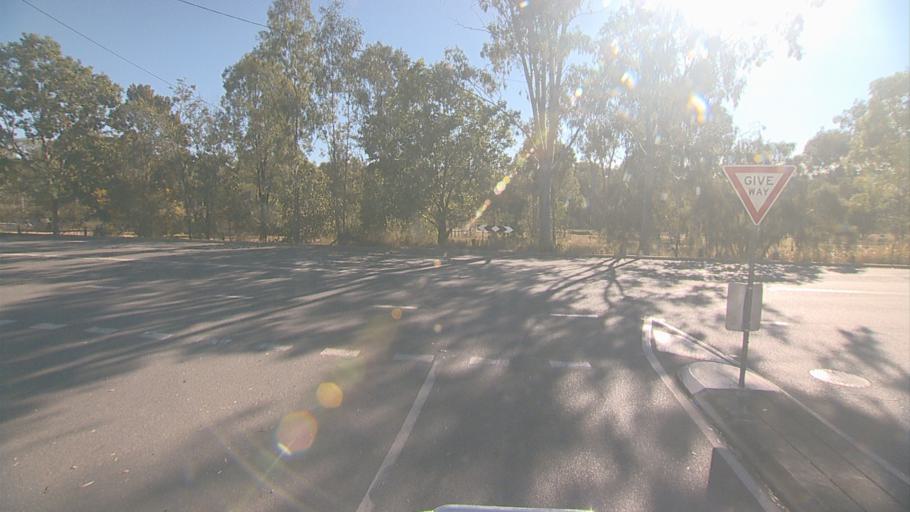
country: AU
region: Queensland
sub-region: Logan
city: North Maclean
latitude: -27.8147
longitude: 152.9888
